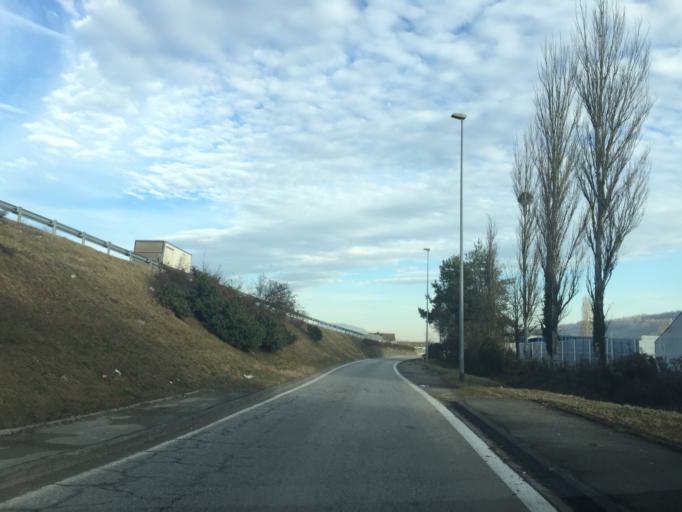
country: FR
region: Rhone-Alpes
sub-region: Departement de la Savoie
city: La Motte-Servolex
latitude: 45.6168
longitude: 5.8845
